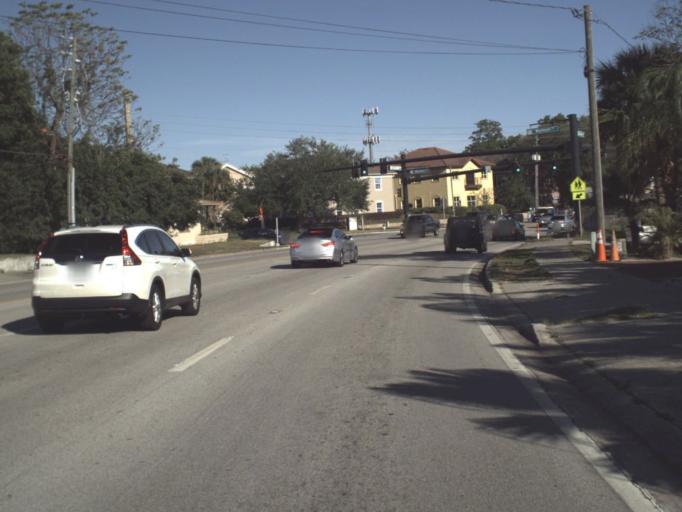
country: US
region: Florida
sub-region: Orange County
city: Fairview Shores
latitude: 28.5953
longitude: -81.3867
